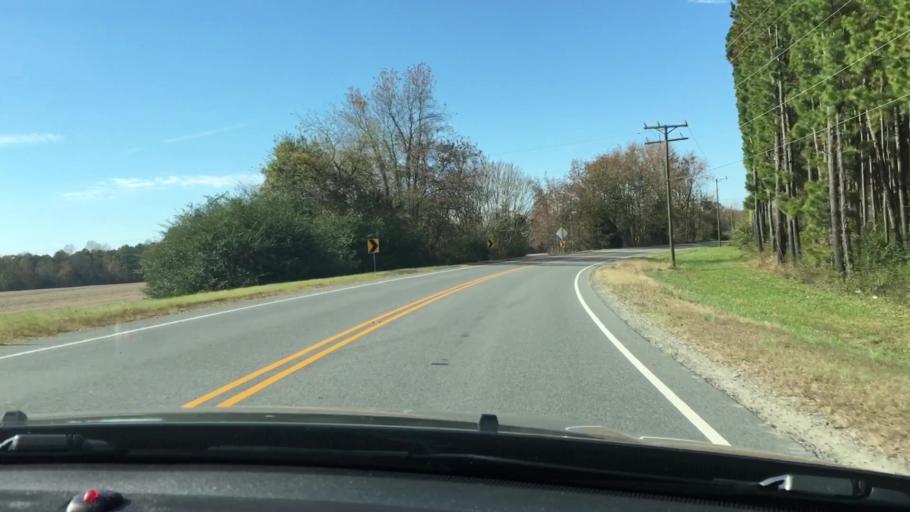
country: US
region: Virginia
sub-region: King and Queen County
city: King and Queen Court House
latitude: 37.5918
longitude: -76.8970
